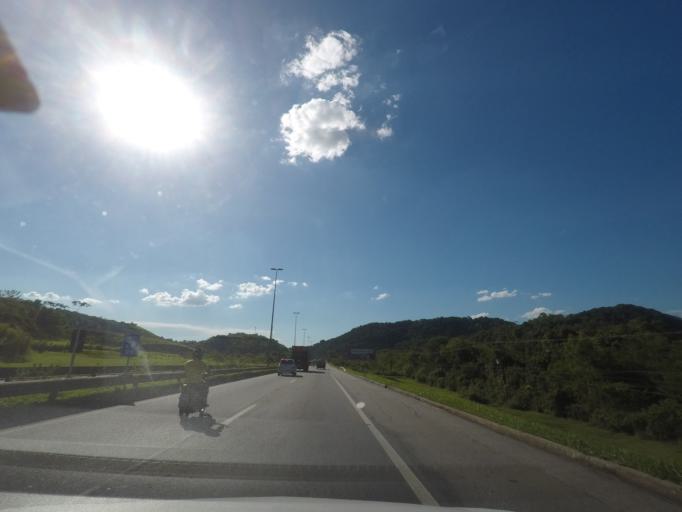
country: BR
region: Rio de Janeiro
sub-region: Petropolis
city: Petropolis
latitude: -22.6567
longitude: -43.1353
